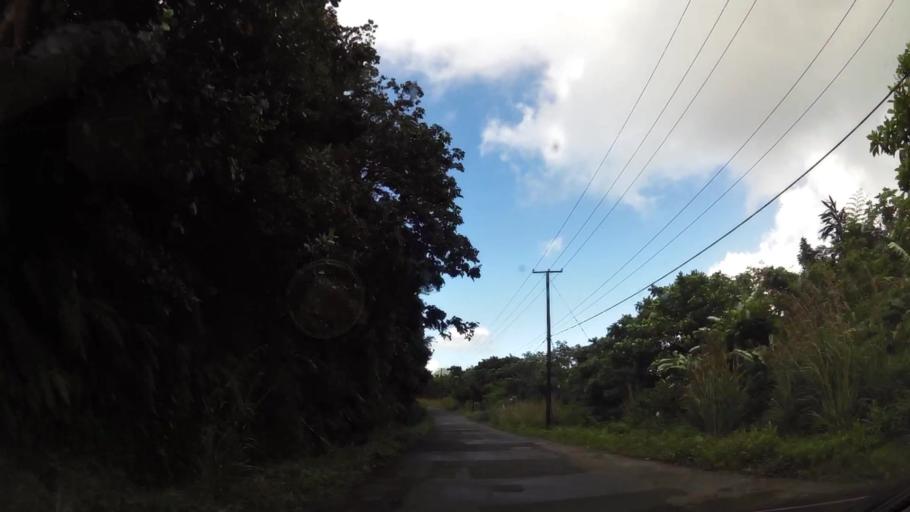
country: DM
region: Saint Paul
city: Pont Casse
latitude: 15.3918
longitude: -61.3264
